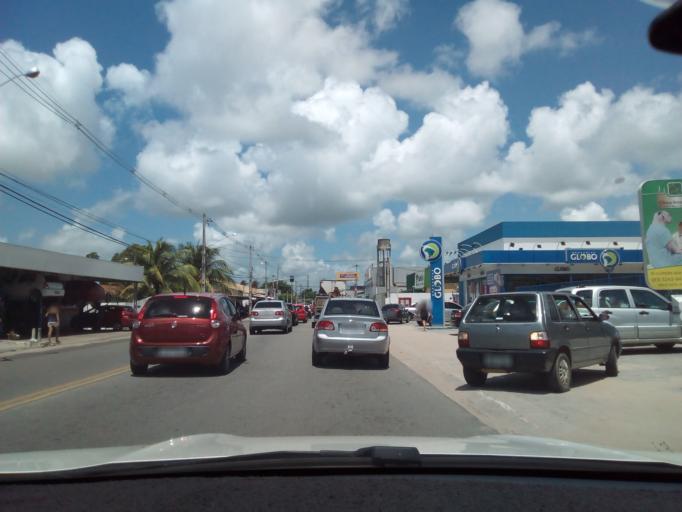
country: BR
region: Paraiba
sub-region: Joao Pessoa
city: Joao Pessoa
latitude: -7.1765
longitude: -34.8739
